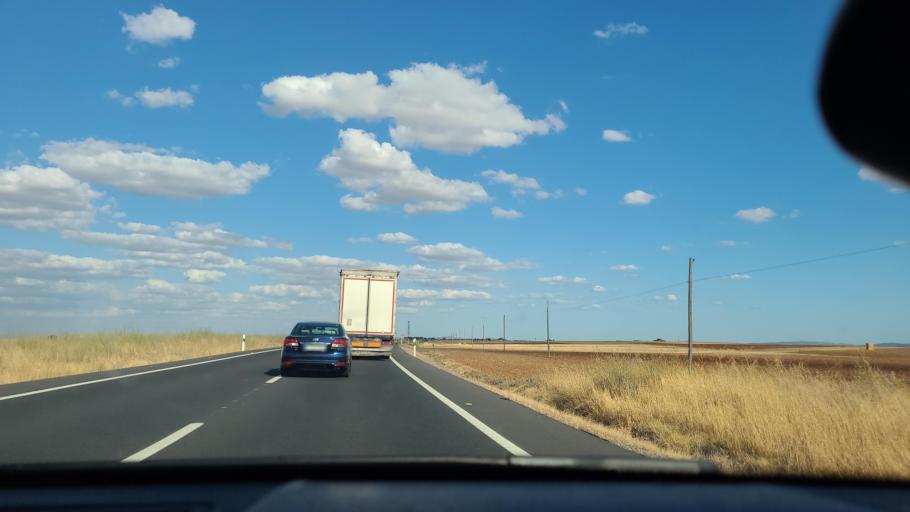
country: ES
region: Extremadura
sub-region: Provincia de Badajoz
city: Azuaga
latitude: 38.2644
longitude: -5.7404
